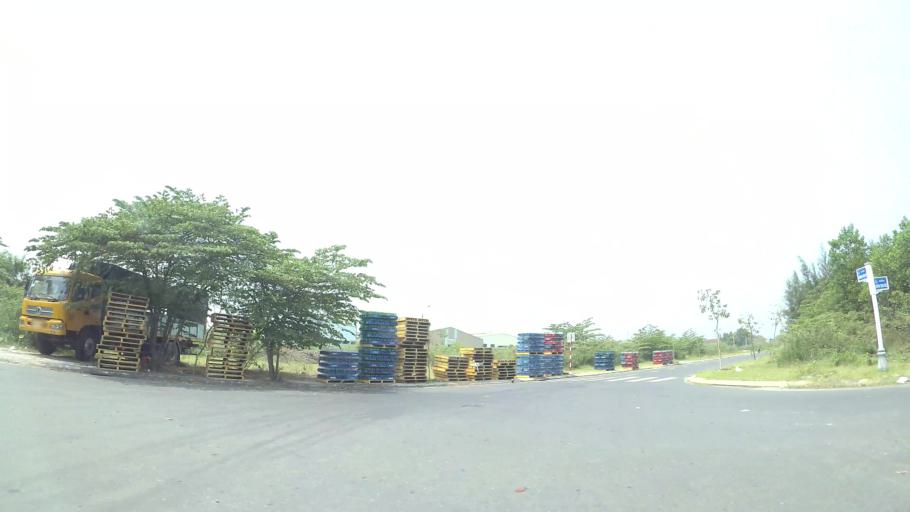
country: VN
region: Da Nang
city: Cam Le
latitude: 15.9843
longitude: 108.2068
